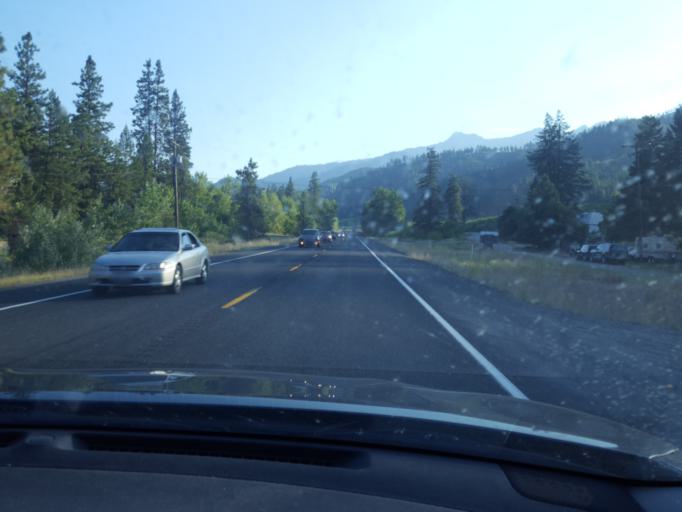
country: US
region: Washington
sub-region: Chelan County
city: Leavenworth
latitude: 47.5499
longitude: -120.6089
